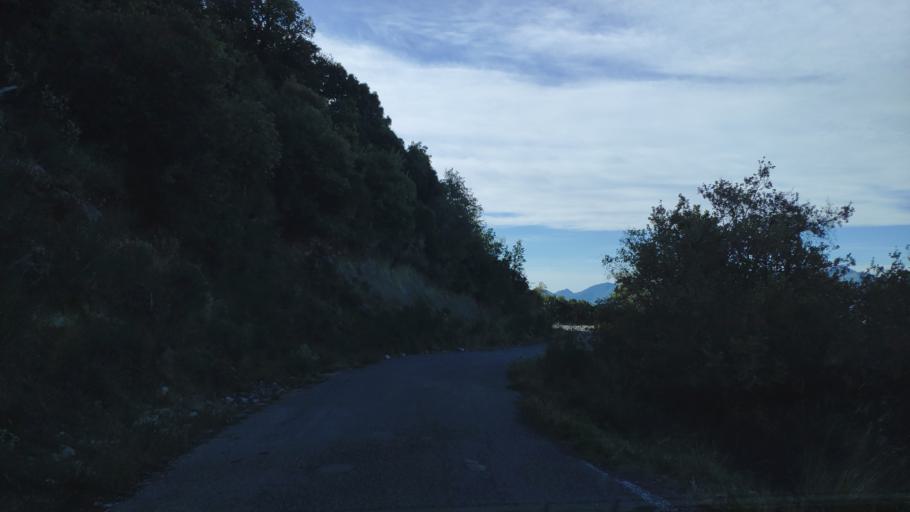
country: GR
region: Peloponnese
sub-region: Nomos Arkadias
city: Dimitsana
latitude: 37.5533
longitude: 22.0594
